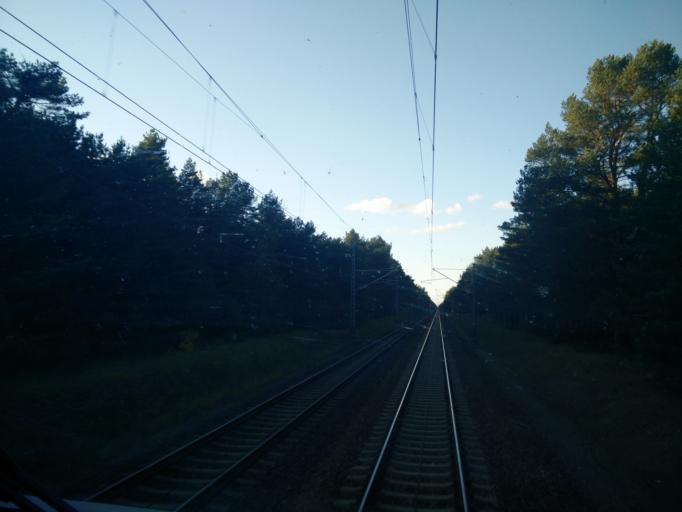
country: DE
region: Brandenburg
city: Dreetz
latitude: 52.8005
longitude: 12.5285
